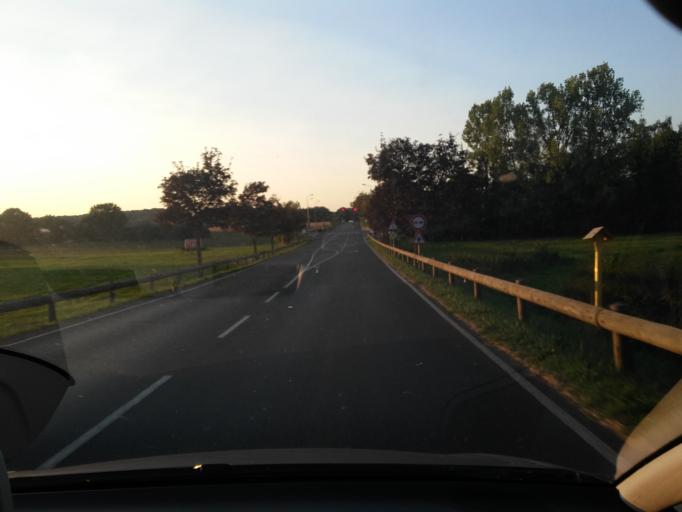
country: LU
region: Luxembourg
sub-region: Canton d'Esch-sur-Alzette
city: Frisange
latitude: 49.5322
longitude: 6.1805
